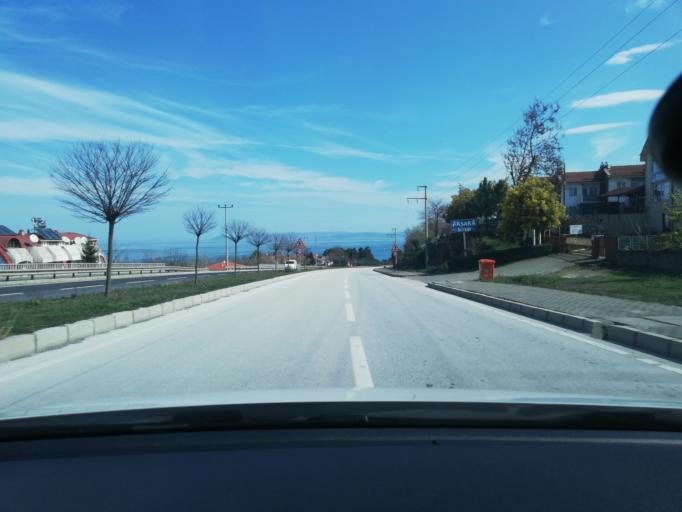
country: TR
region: Duzce
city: Akcakoca
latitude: 41.0917
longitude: 31.1877
